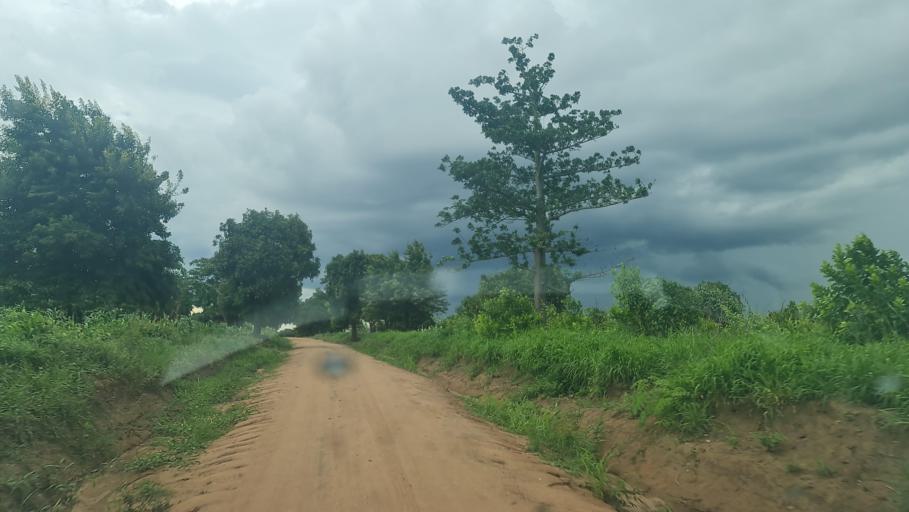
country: MW
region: Southern Region
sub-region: Nsanje District
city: Nsanje
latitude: -17.3797
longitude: 35.5825
